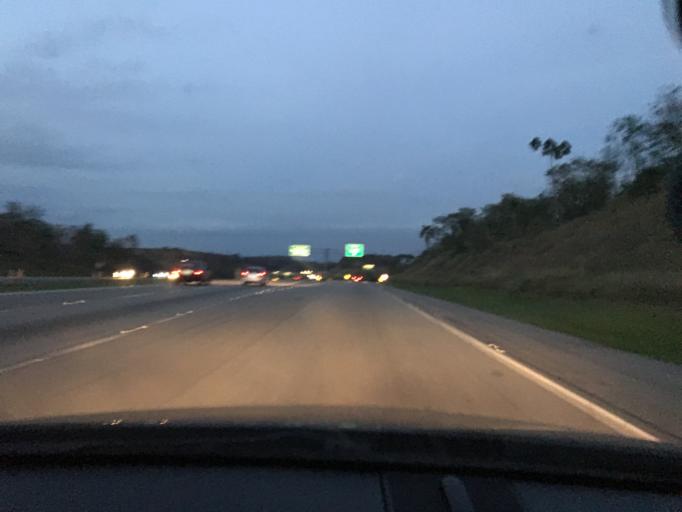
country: BR
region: Sao Paulo
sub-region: Santa Isabel
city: Santa Isabel
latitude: -23.3695
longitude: -46.1349
